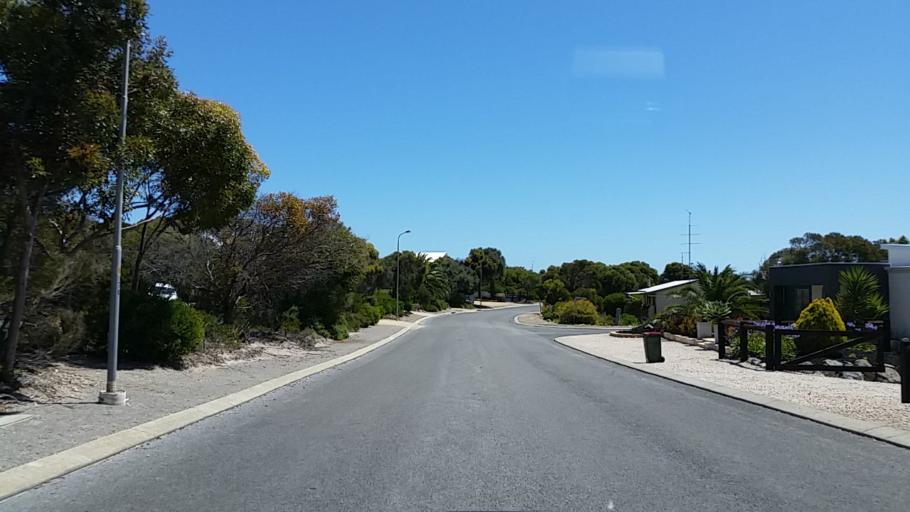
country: AU
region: South Australia
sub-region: Yorke Peninsula
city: Honiton
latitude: -35.2479
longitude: 136.9743
